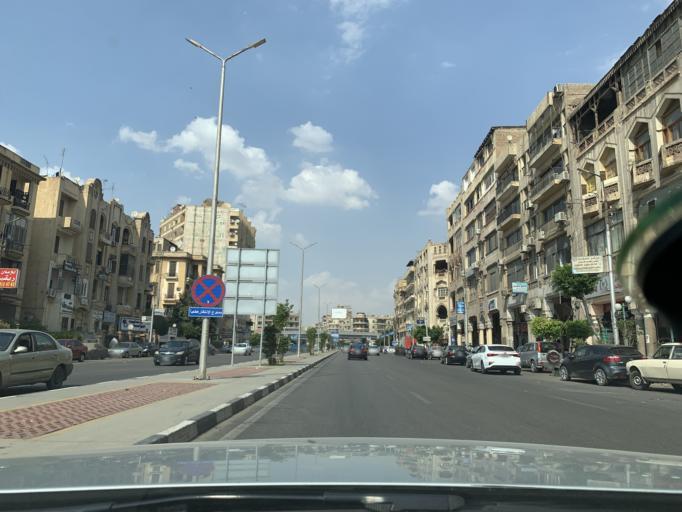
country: EG
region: Muhafazat al Qahirah
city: Cairo
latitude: 30.0968
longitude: 31.3356
